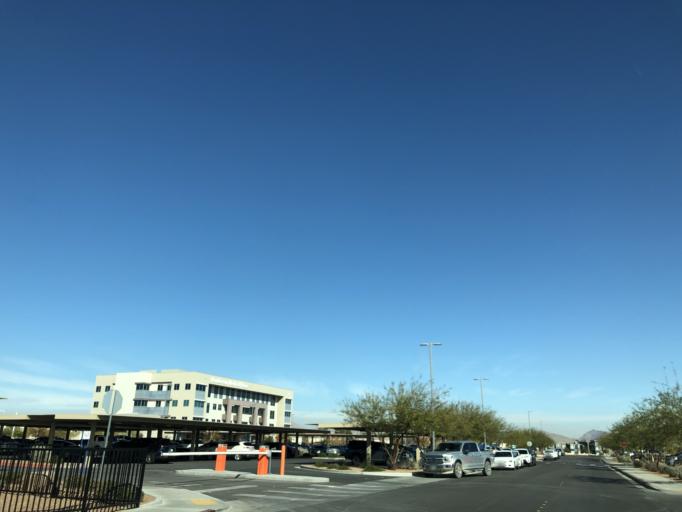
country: US
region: Nevada
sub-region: Clark County
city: Whitney
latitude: 36.0721
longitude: -115.0295
